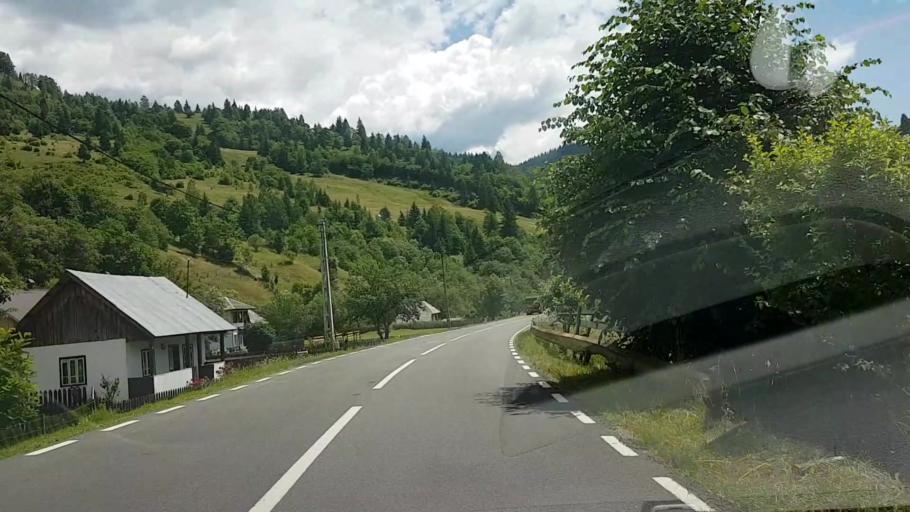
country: RO
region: Suceava
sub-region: Comuna Crucea
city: Crucea
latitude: 47.3910
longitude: 25.5778
